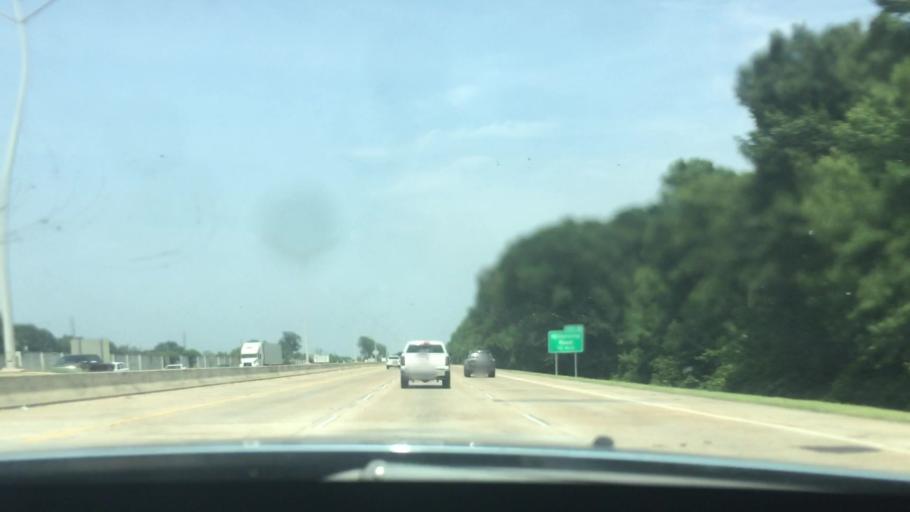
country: US
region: Louisiana
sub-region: East Baton Rouge Parish
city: Westminster
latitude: 30.4338
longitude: -91.0416
